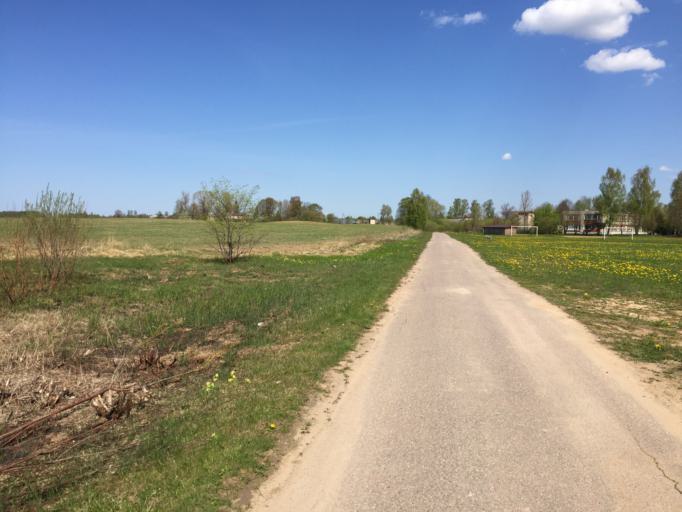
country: LV
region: Saulkrastu
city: Saulkrasti
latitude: 57.3255
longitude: 24.4877
